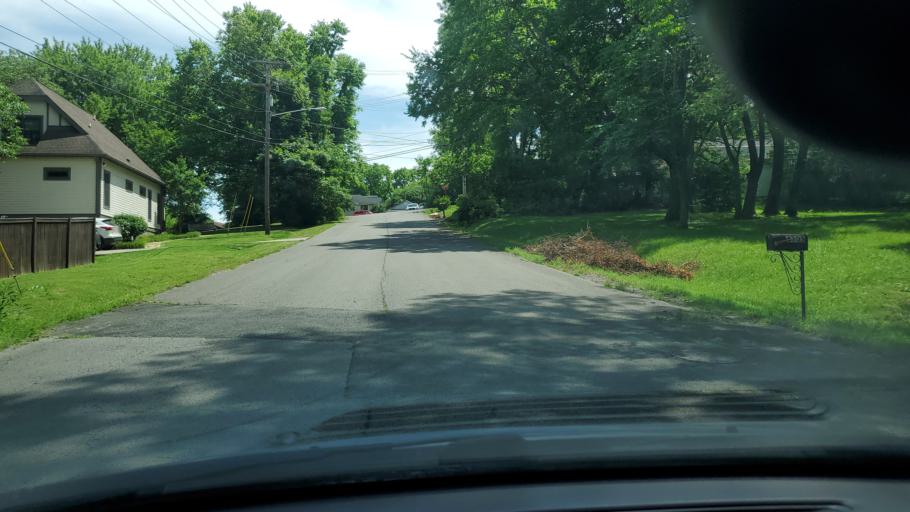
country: US
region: Tennessee
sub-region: Davidson County
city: Nashville
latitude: 36.2290
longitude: -86.7381
